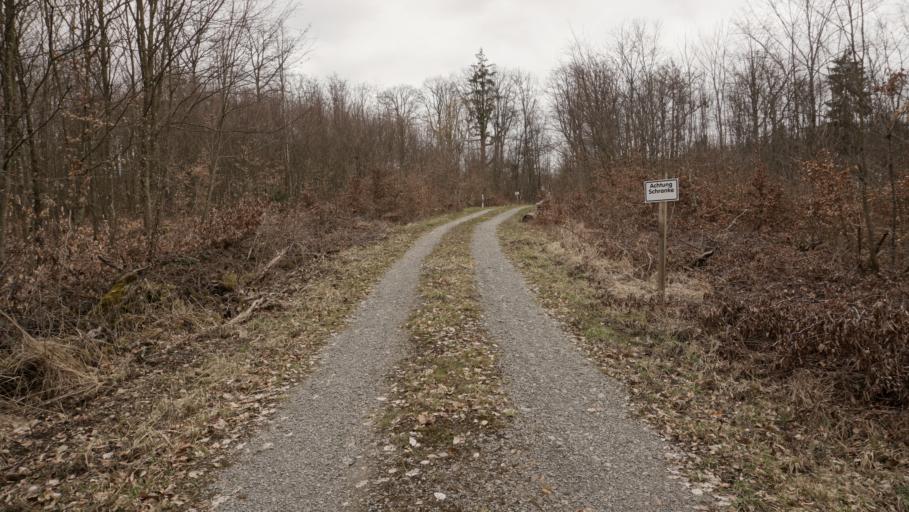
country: DE
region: Baden-Wuerttemberg
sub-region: Karlsruhe Region
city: Mosbach
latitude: 49.3866
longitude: 9.1358
